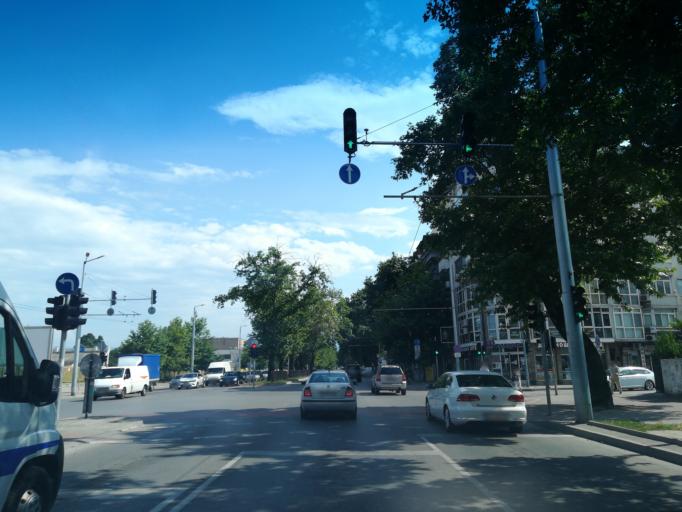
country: BG
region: Plovdiv
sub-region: Obshtina Plovdiv
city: Plovdiv
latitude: 42.1412
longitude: 24.7630
